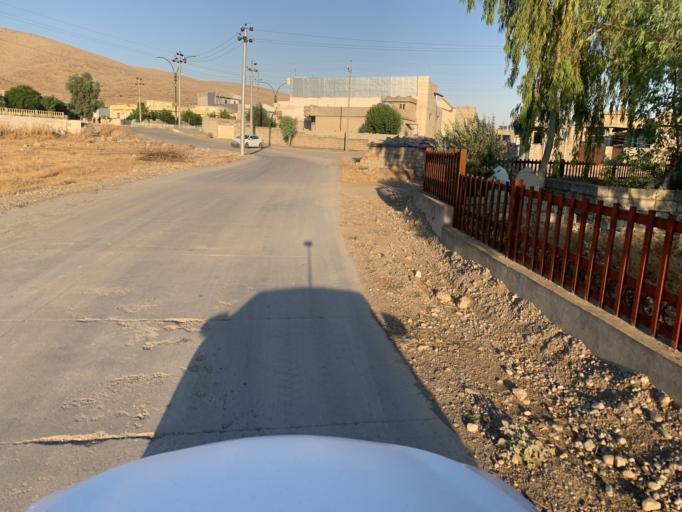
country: IQ
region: As Sulaymaniyah
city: Raniye
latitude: 36.2714
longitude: 44.7596
